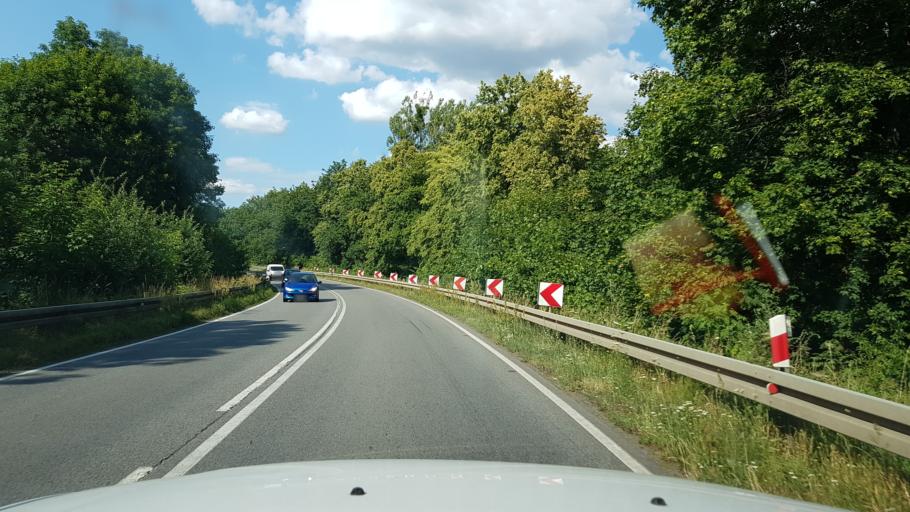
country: PL
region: West Pomeranian Voivodeship
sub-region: Powiat gryfinski
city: Stare Czarnowo
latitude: 53.3012
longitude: 14.7928
